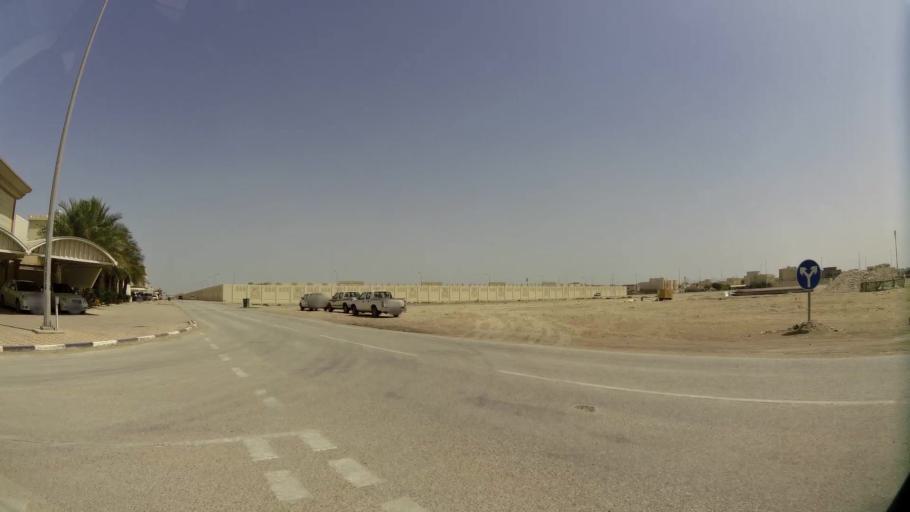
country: QA
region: Baladiyat Umm Salal
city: Umm Salal Muhammad
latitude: 25.3877
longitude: 51.4539
